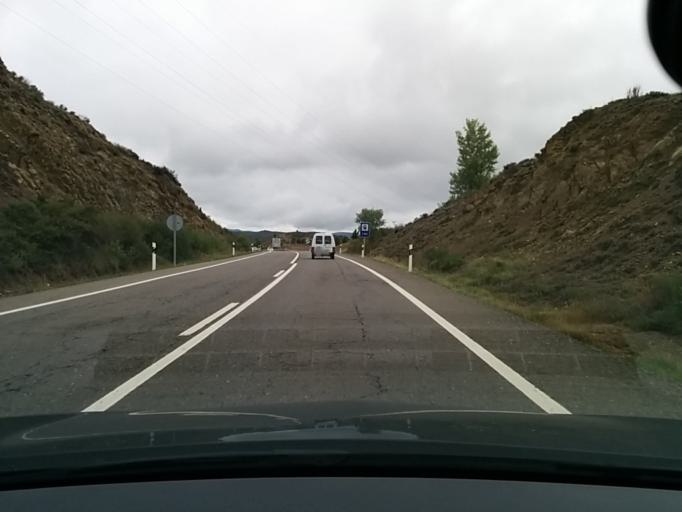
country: ES
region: Aragon
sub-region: Provincia de Huesca
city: Sabinanigo
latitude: 42.4245
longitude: -0.3959
